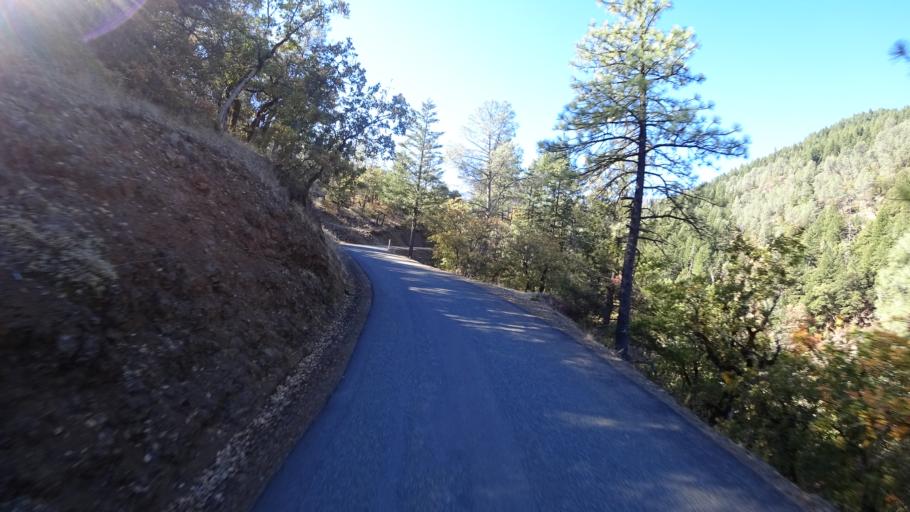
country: US
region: California
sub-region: Humboldt County
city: Willow Creek
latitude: 41.1569
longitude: -123.2092
